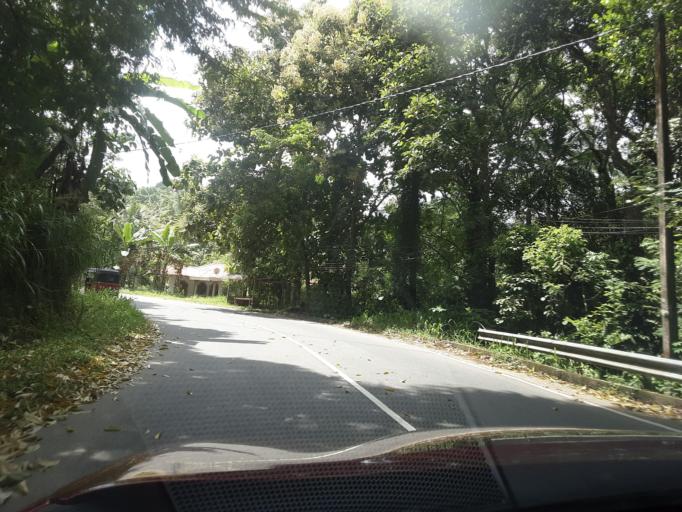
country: LK
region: Uva
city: Monaragala
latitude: 6.8952
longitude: 81.2543
